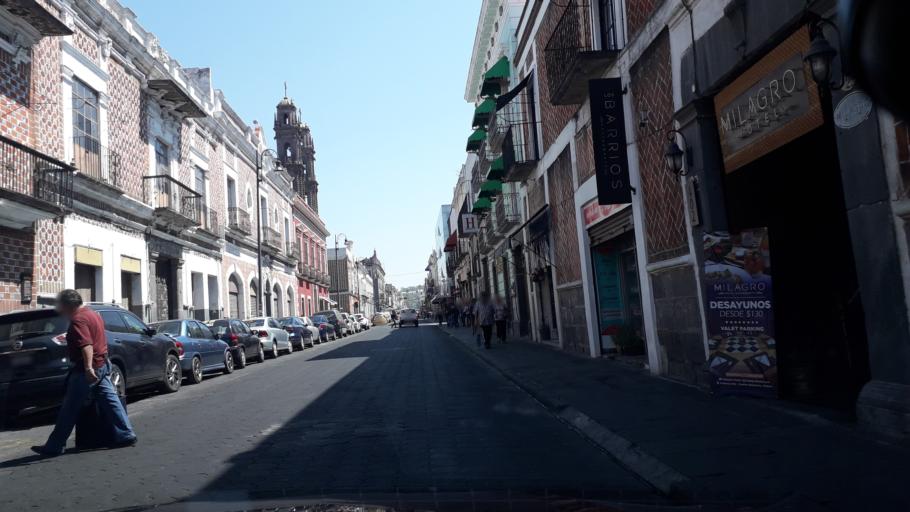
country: MX
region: Puebla
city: Puebla
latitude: 19.0445
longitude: -98.1947
